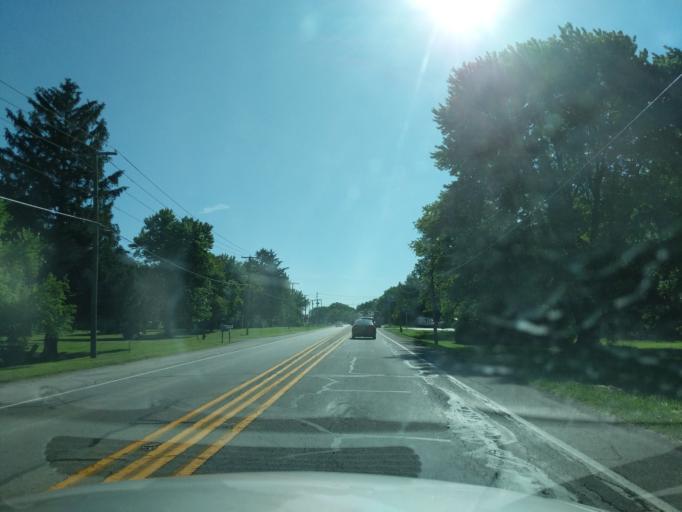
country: US
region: Indiana
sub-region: Madison County
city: Chesterfield
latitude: 40.1147
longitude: -85.5798
